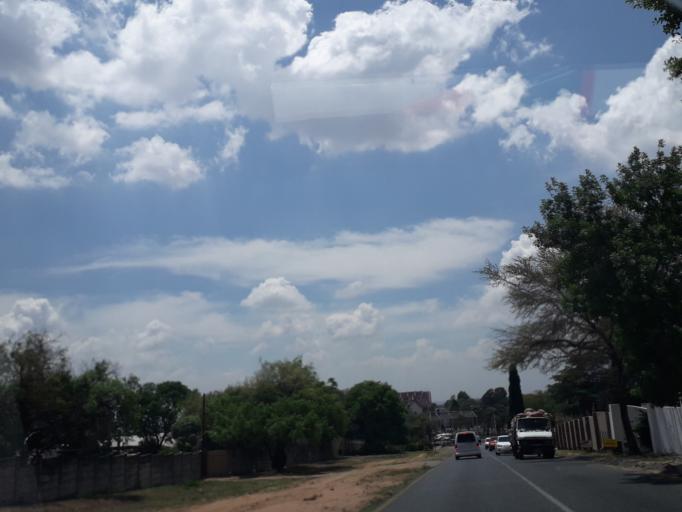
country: ZA
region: Gauteng
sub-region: West Rand District Municipality
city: Muldersdriseloop
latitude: -26.0727
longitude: 27.9345
